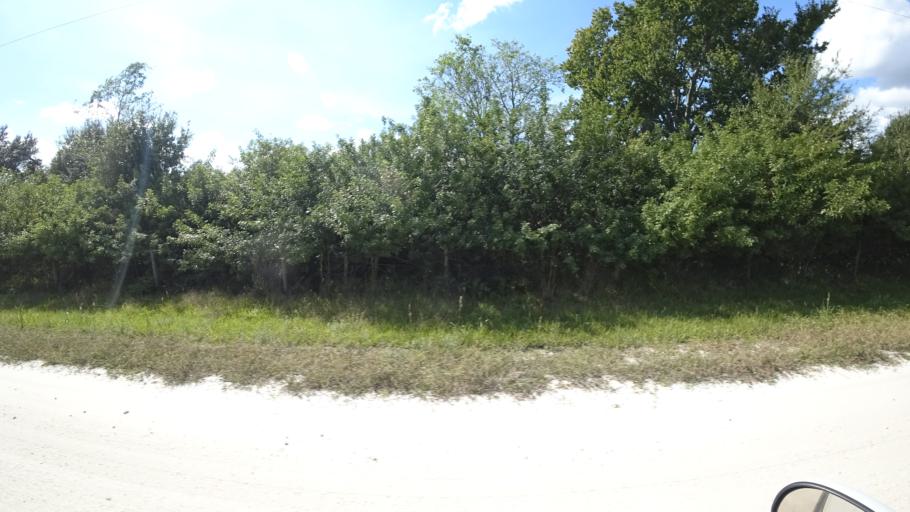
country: US
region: Florida
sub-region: DeSoto County
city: Arcadia
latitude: 27.3213
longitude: -82.0805
